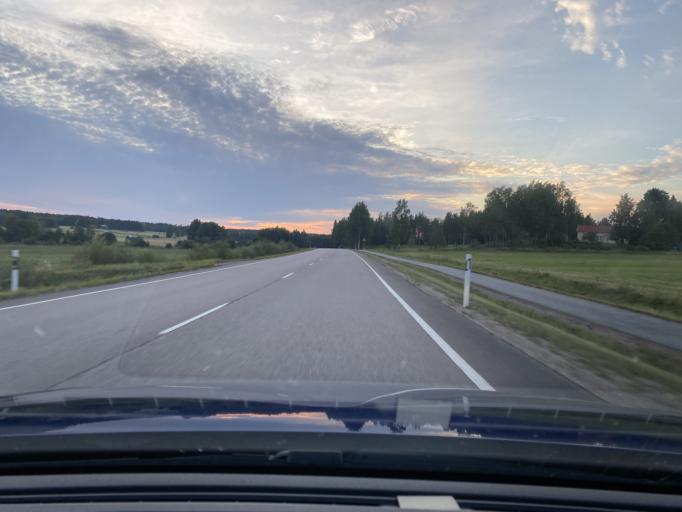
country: FI
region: Satakunta
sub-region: Pohjois-Satakunta
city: Honkajoki
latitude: 61.8729
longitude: 22.3040
